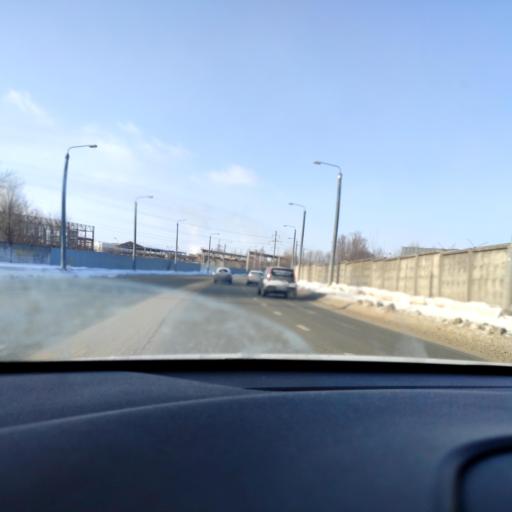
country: RU
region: Tatarstan
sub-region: Gorod Kazan'
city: Kazan
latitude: 55.8513
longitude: 49.1273
